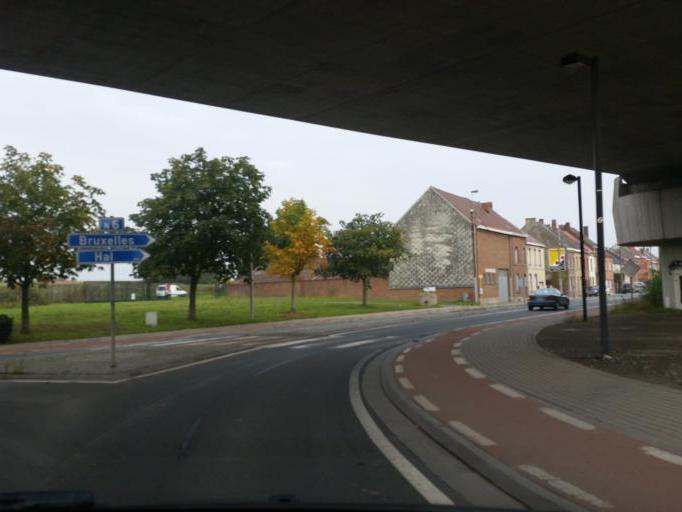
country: BE
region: Wallonia
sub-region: Province du Brabant Wallon
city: Tubize
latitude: 50.7060
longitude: 4.2110
